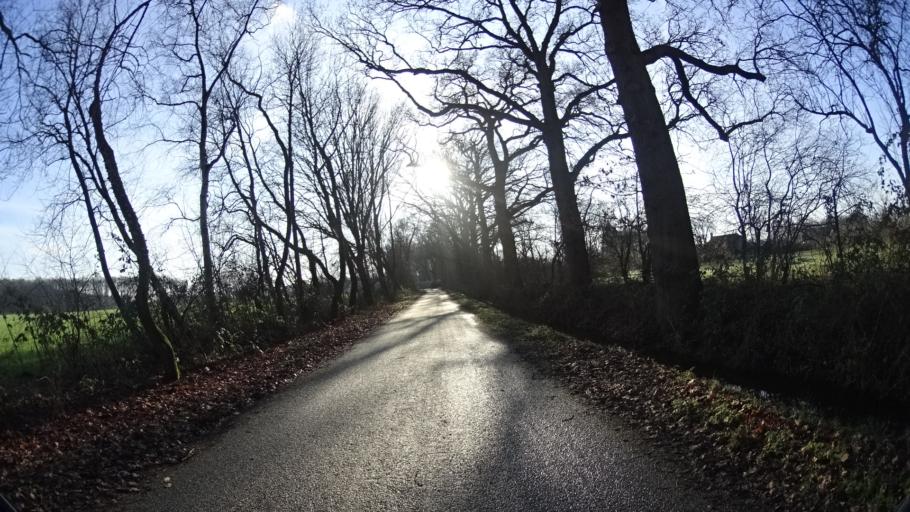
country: NL
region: Gelderland
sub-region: Gemeente Ede
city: Otterlo
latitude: 52.0478
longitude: 5.7322
